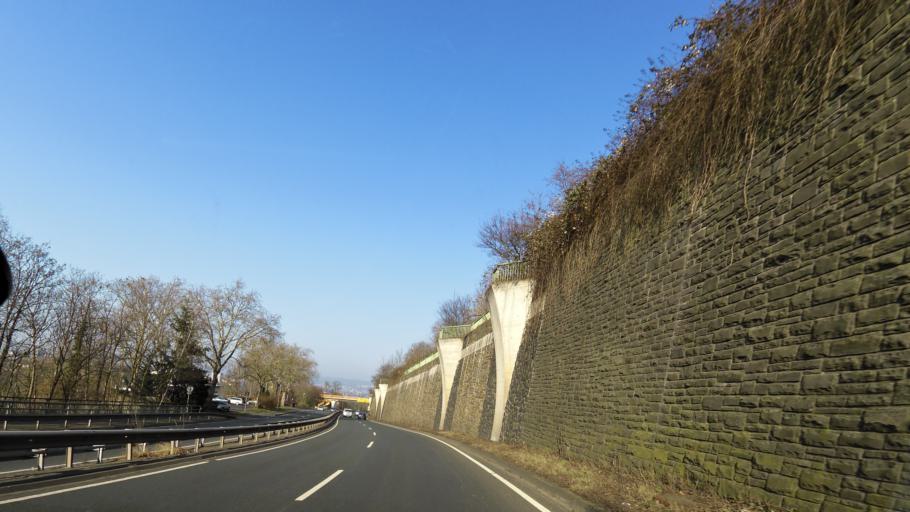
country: DE
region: Rheinland-Pfalz
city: Koblenz
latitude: 50.3470
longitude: 7.6074
